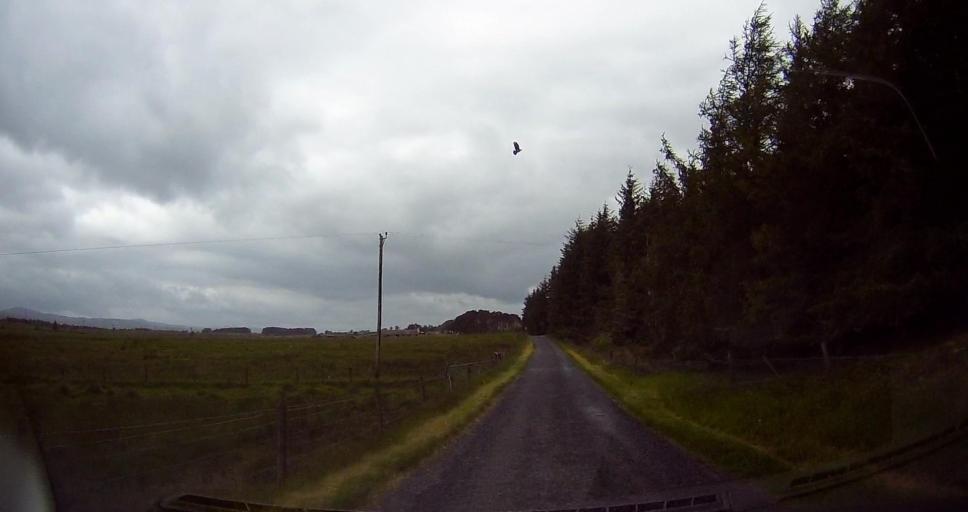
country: GB
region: Scotland
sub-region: Highland
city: Alness
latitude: 58.0677
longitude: -4.4263
